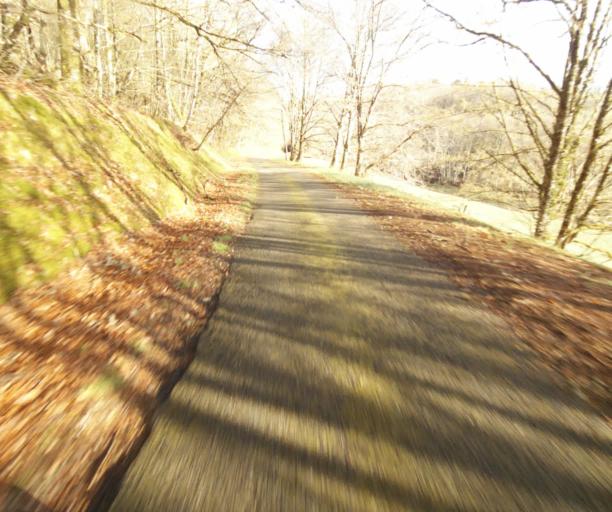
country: FR
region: Limousin
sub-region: Departement de la Correze
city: Correze
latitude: 45.2959
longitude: 1.8552
